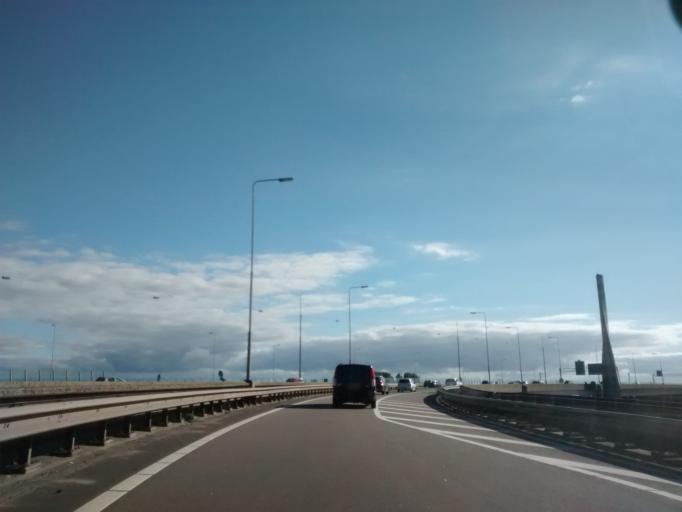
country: NL
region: North Holland
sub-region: Gemeente Diemen
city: Diemen
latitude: 52.3655
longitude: 4.9701
